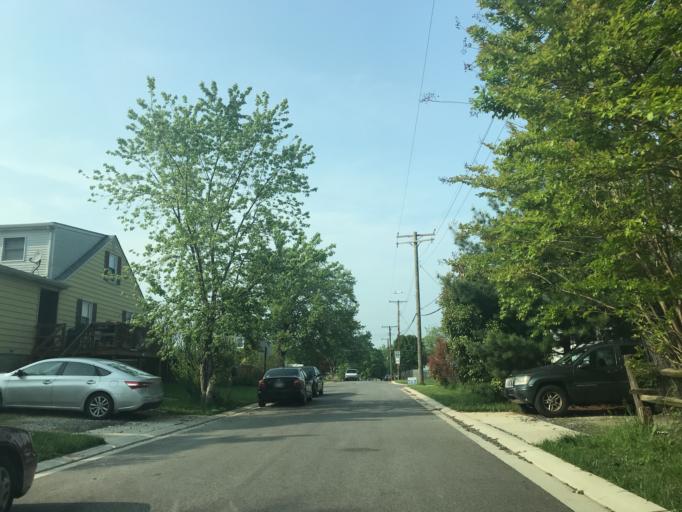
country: US
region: Maryland
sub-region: Baltimore County
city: Parkville
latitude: 39.3830
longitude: -76.5608
